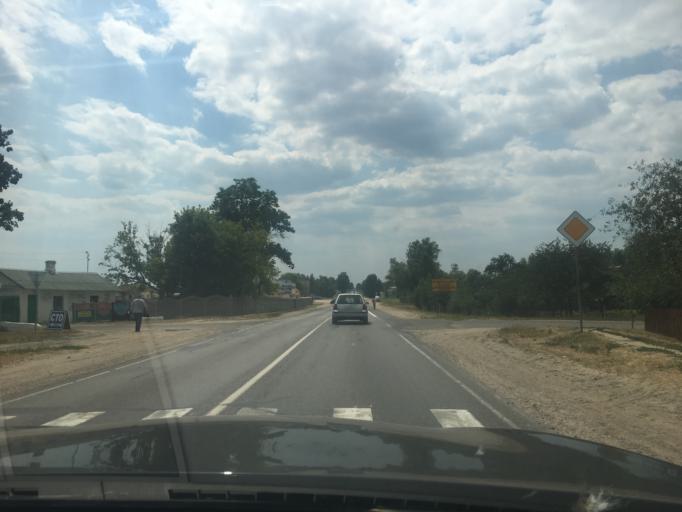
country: BY
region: Brest
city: Pruzhany
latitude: 52.5515
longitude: 24.4705
